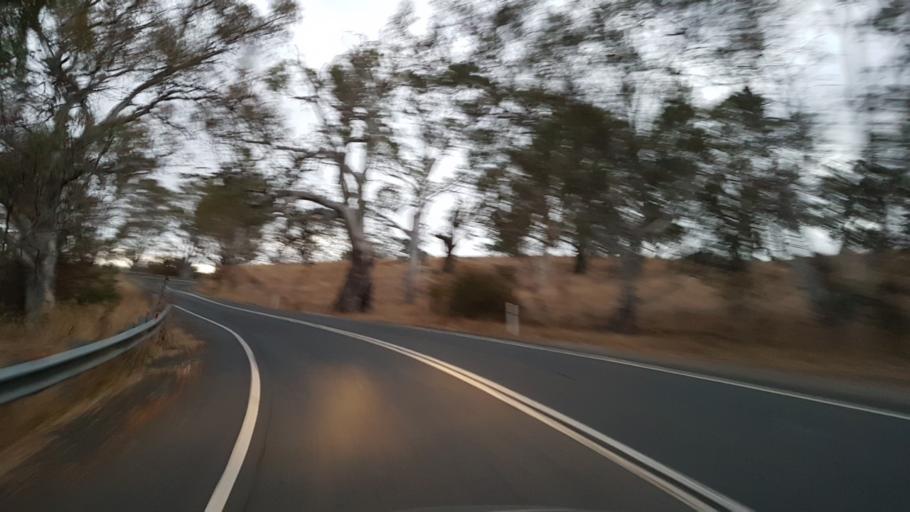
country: AU
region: South Australia
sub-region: Mount Barker
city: Nairne
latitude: -35.0347
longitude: 138.9536
